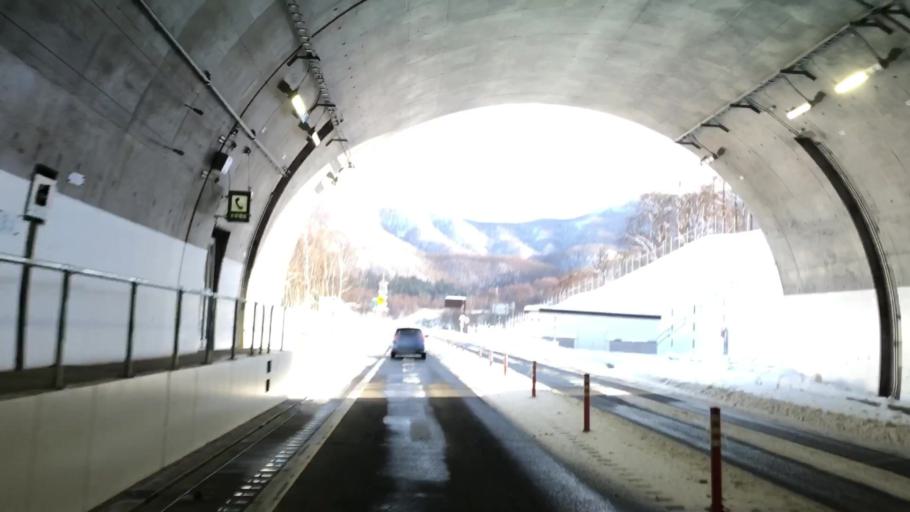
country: JP
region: Hokkaido
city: Otaru
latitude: 43.1753
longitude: 140.9753
